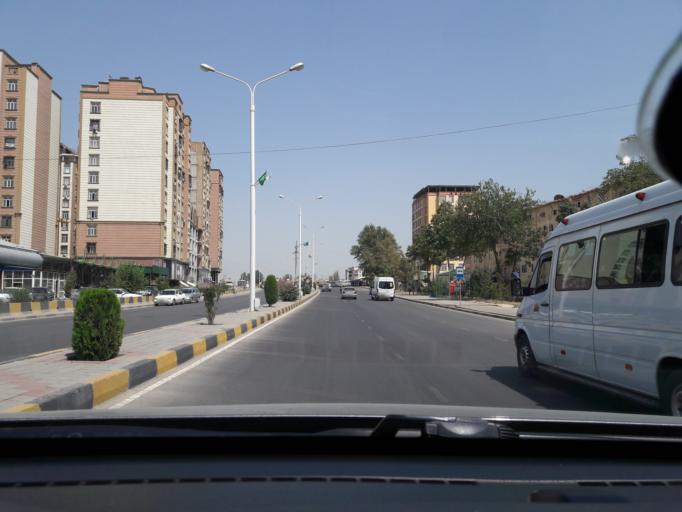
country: TJ
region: Dushanbe
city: Dushanbe
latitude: 38.5881
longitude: 68.7192
